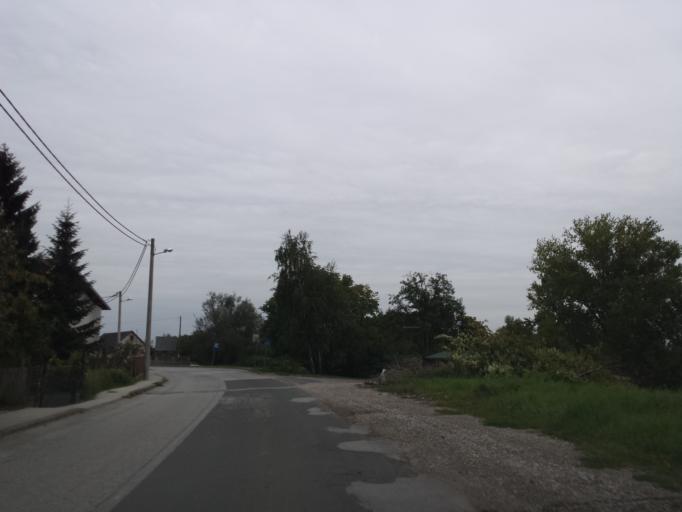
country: HR
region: Grad Zagreb
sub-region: Sesvete
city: Sesvete
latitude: 45.7934
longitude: 16.1214
